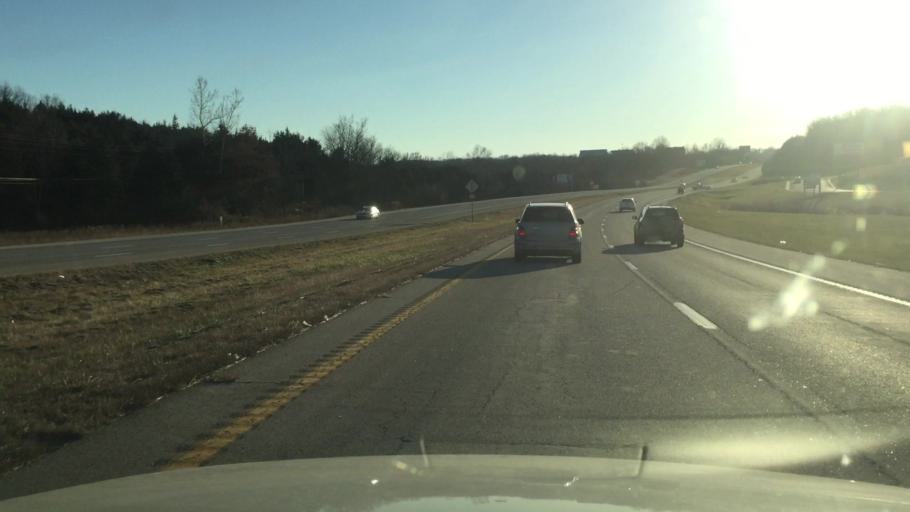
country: US
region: Missouri
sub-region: Cole County
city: Wardsville
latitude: 38.5293
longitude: -92.2208
